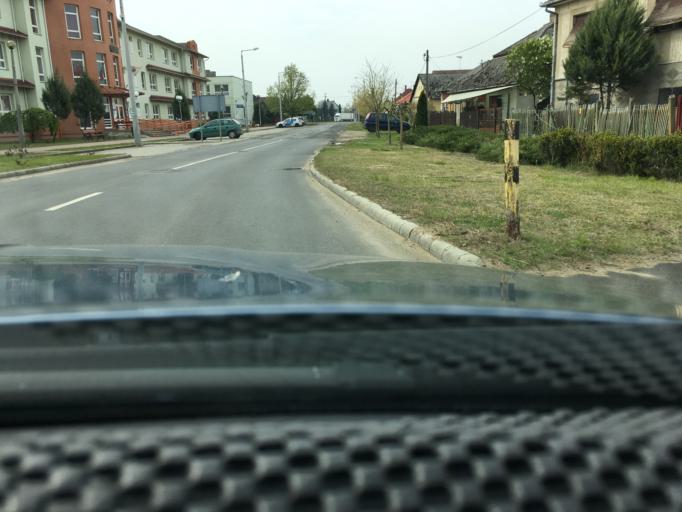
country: HU
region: Szabolcs-Szatmar-Bereg
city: Nyirlugos
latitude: 47.6935
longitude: 22.0388
